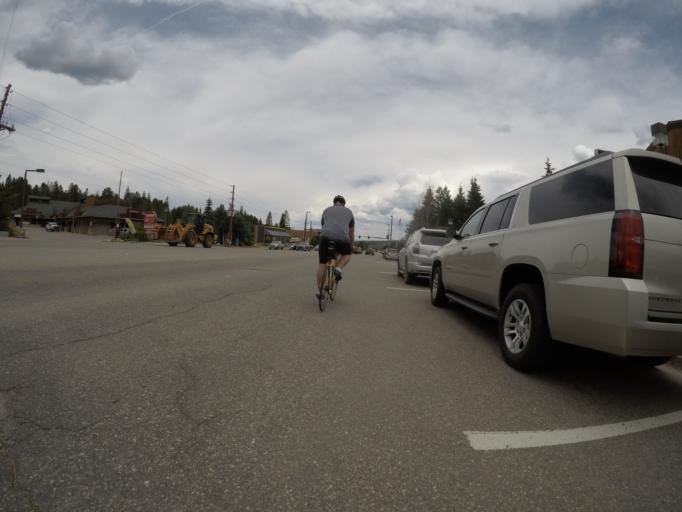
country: US
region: Colorado
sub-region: Grand County
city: Fraser
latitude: 39.9184
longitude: -105.7845
